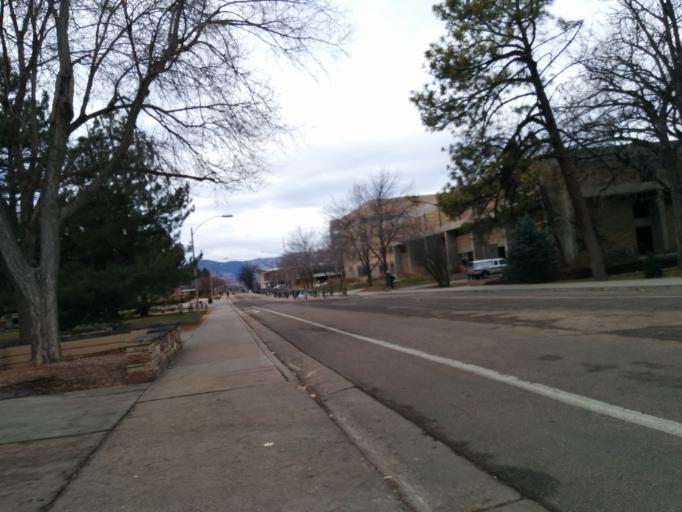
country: US
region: Colorado
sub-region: Larimer County
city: Fort Collins
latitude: 40.5737
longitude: -105.0815
